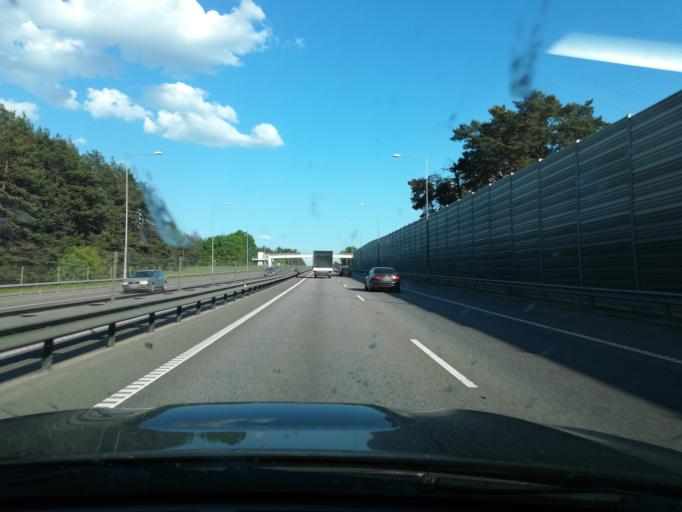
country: LT
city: Grigiskes
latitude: 54.6723
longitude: 25.0960
